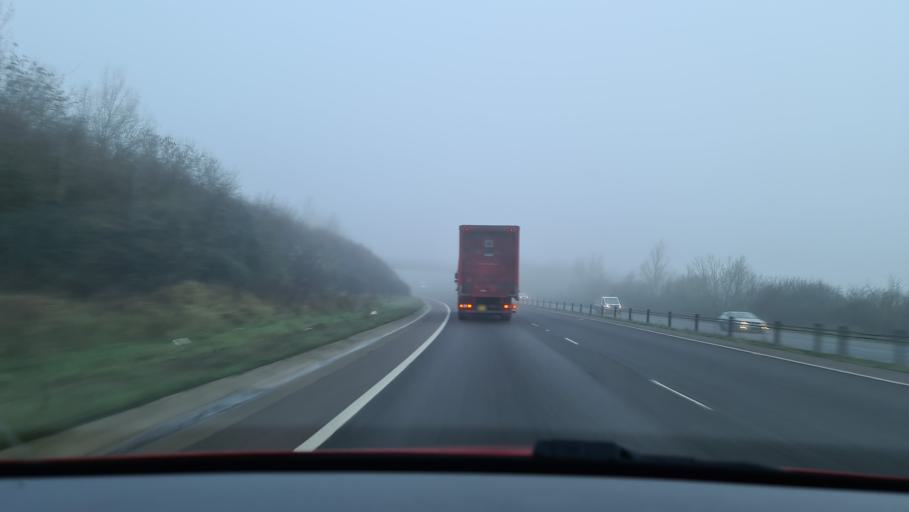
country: GB
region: England
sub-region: Buckinghamshire
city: Aston Clinton
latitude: 51.8118
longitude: -0.7155
